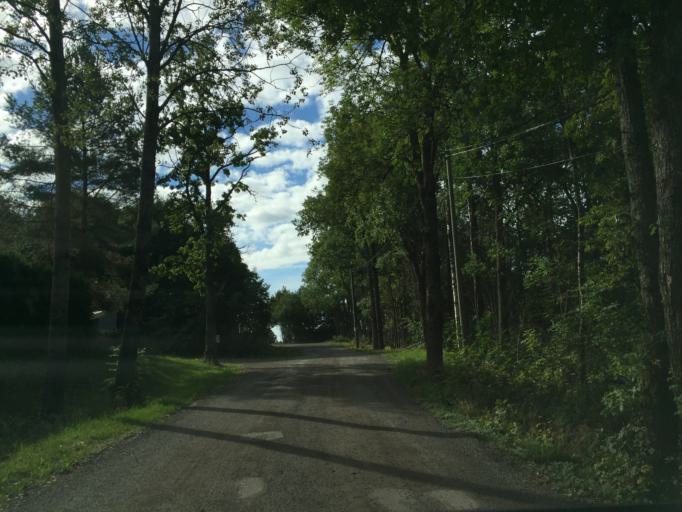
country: NO
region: Vestfold
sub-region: Holmestrand
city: Gullhaug
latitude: 59.4708
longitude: 10.1942
